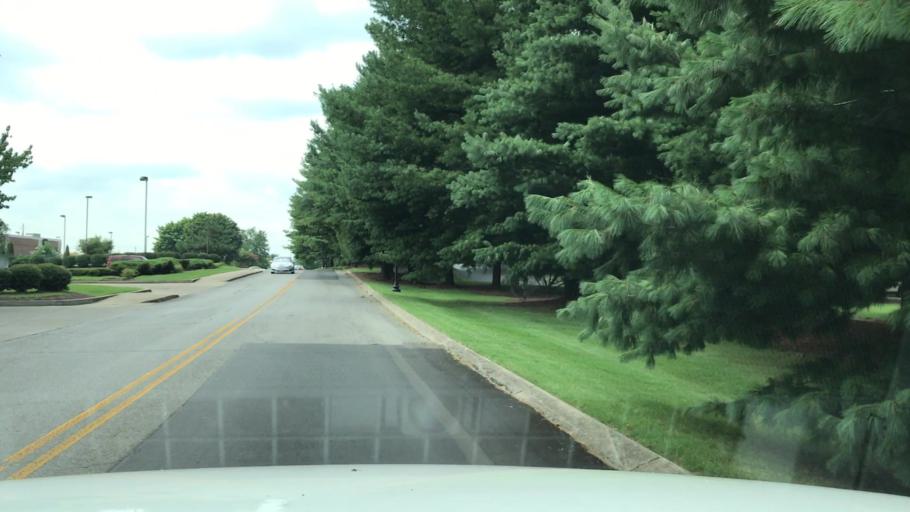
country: US
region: Tennessee
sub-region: Sumner County
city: Gallatin
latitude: 36.3784
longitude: -86.4714
